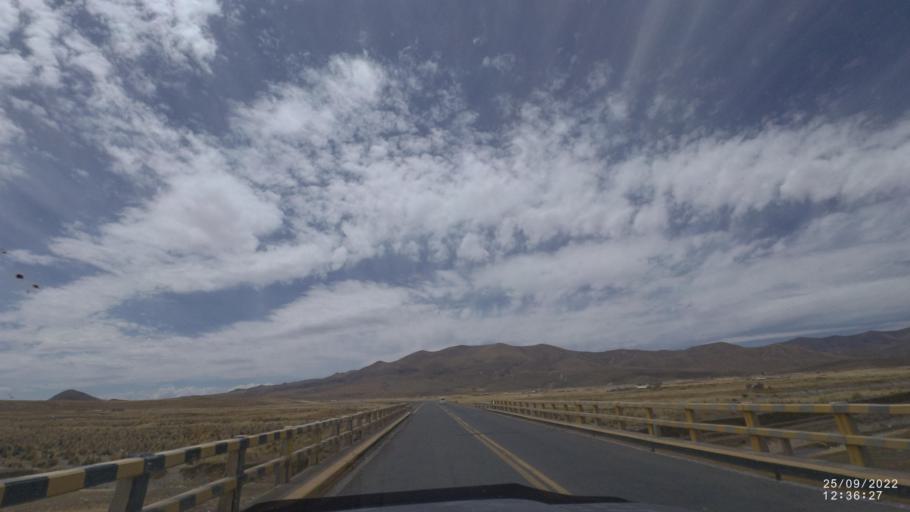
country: BO
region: Oruro
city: Machacamarca
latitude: -18.1640
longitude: -66.9886
